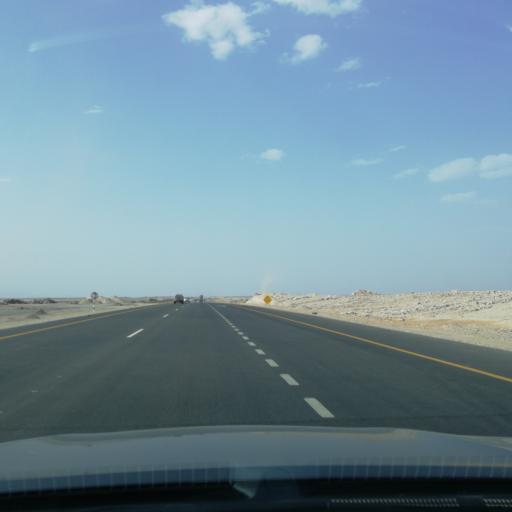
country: OM
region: Muhafazat ad Dakhiliyah
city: Adam
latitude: 22.0574
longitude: 57.5126
